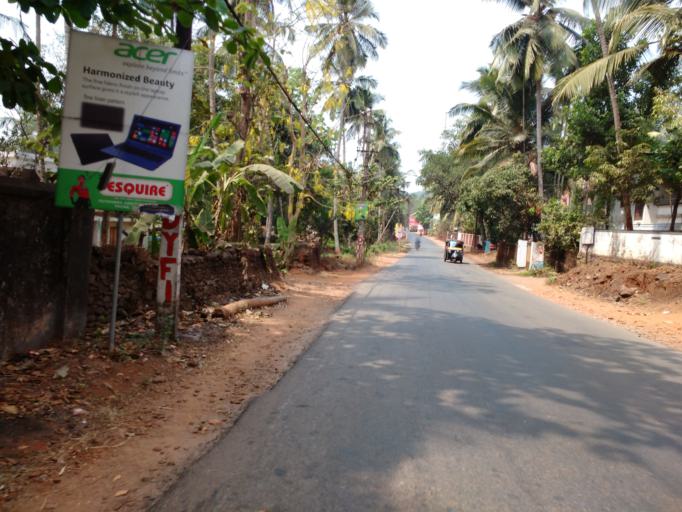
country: IN
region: Kerala
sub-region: Kozhikode
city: Kunnamangalam
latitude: 11.2824
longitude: 75.8489
